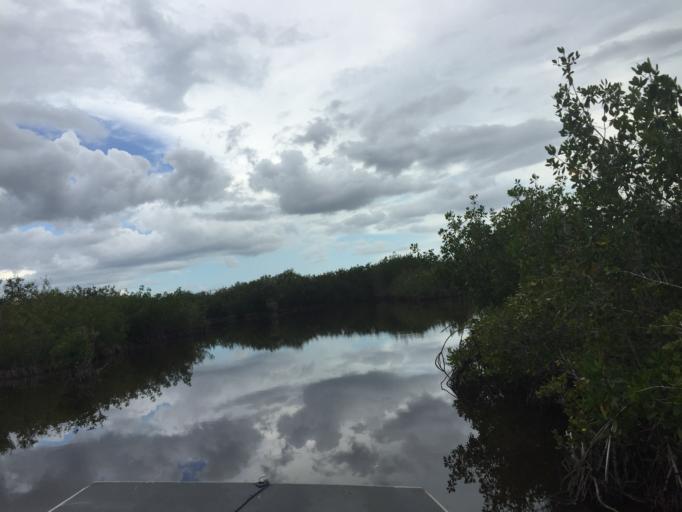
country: US
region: Florida
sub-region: Collier County
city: Marco
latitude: 25.9065
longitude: -81.3691
